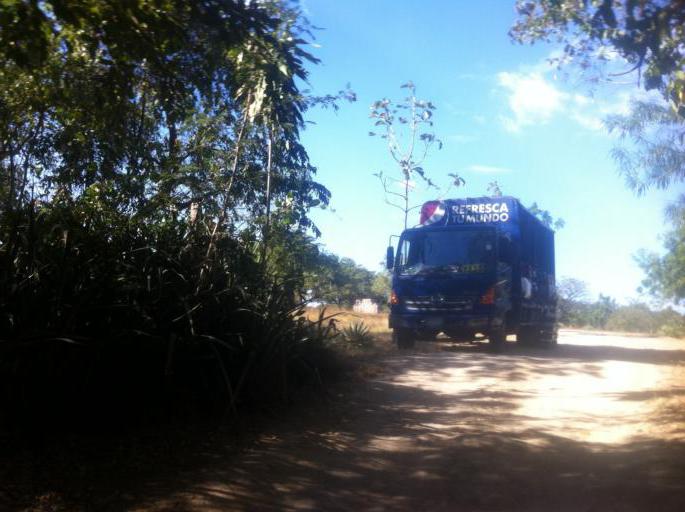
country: NI
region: Managua
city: Carlos Fonseca Amador
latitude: 11.8998
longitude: -86.6077
